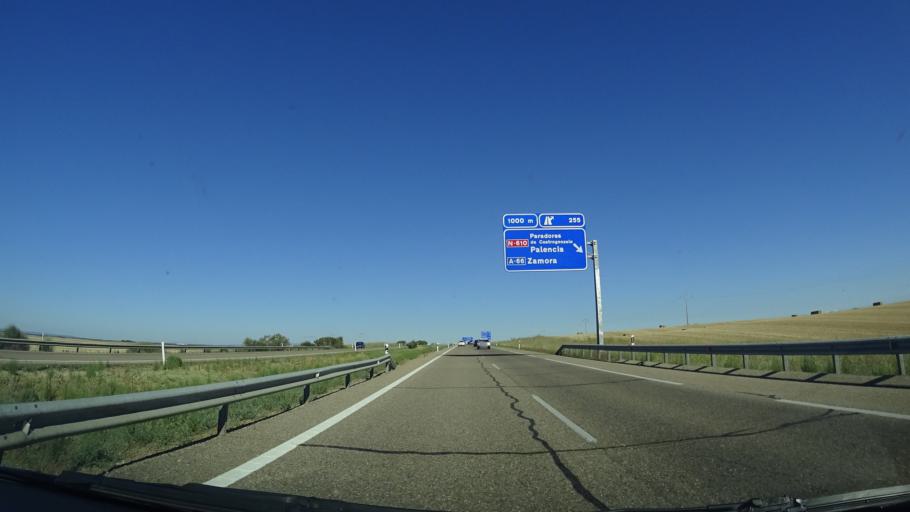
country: ES
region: Castille and Leon
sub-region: Provincia de Zamora
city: San Esteban del Molar
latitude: 41.9560
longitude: -5.5752
